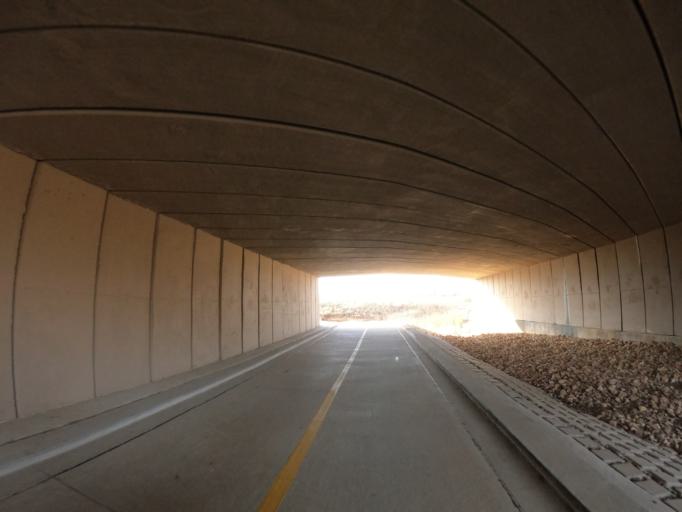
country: US
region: Arkansas
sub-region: Benton County
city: Lowell
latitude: 36.2917
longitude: -94.1716
